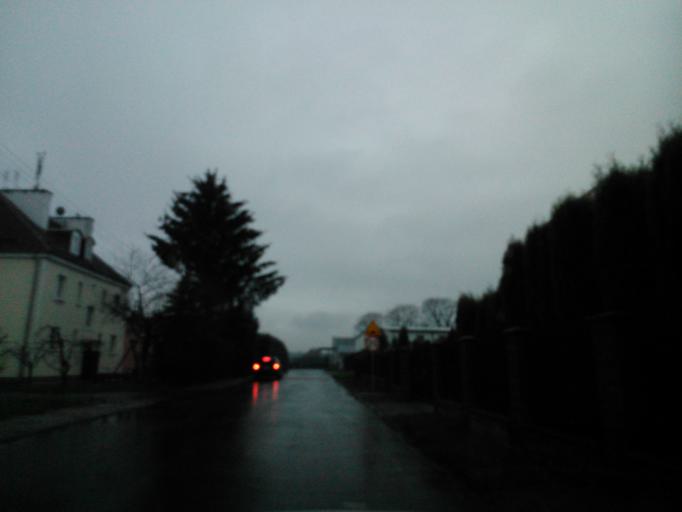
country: PL
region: Lublin Voivodeship
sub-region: Powiat krasnicki
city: Szastarka
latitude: 50.8994
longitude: 22.2882
